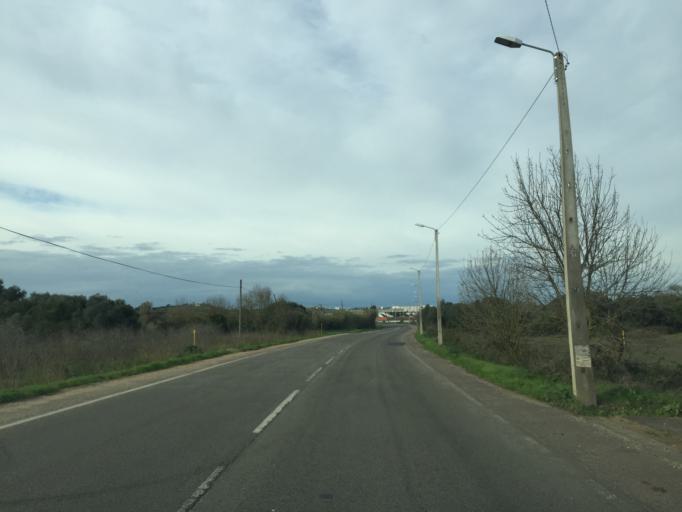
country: PT
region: Lisbon
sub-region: Sintra
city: Almargem
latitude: 38.8697
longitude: -9.2907
